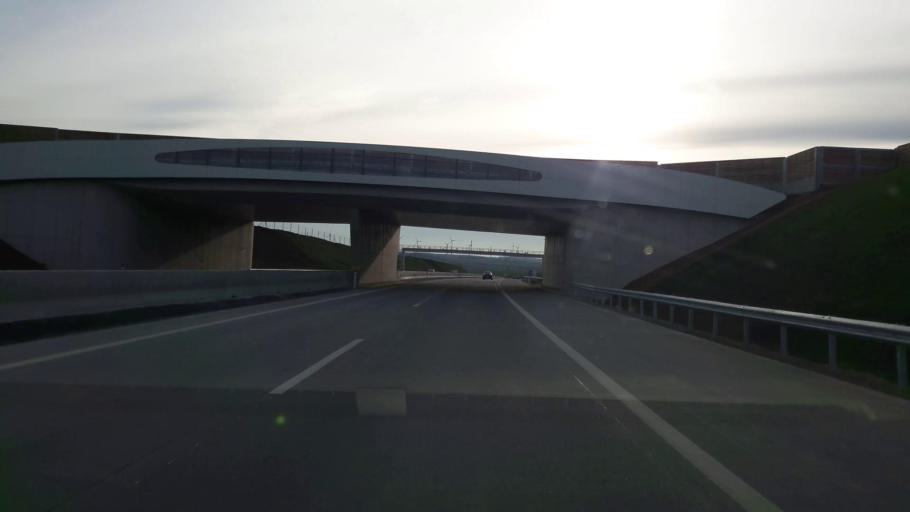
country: AT
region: Lower Austria
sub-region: Politischer Bezirk Mistelbach
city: Wilfersdorf
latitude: 48.5871
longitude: 16.6276
